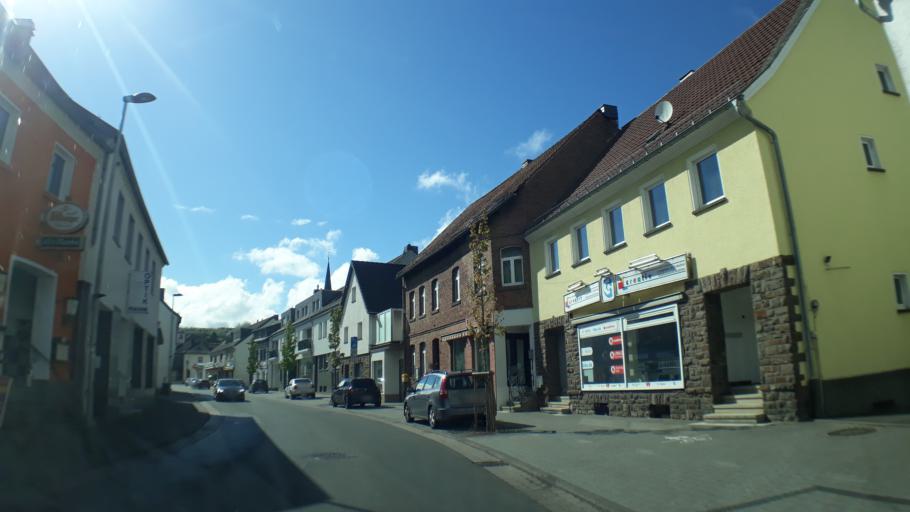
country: DE
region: North Rhine-Westphalia
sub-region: Regierungsbezirk Koln
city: Hellenthal
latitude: 50.4908
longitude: 6.4409
